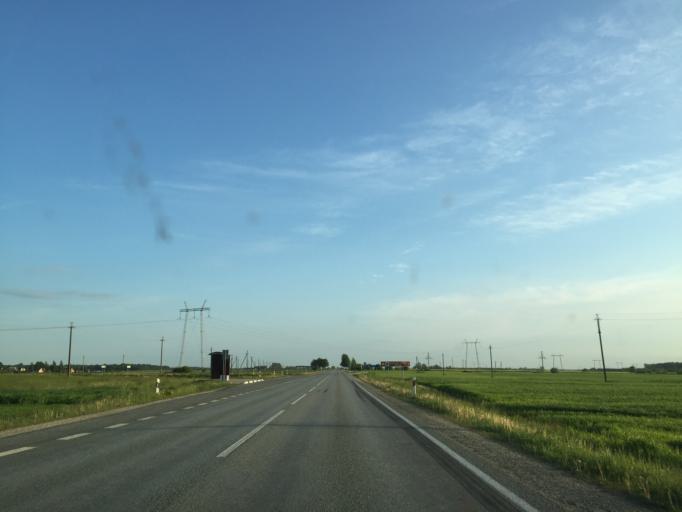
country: LT
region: Siauliu apskritis
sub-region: Joniskis
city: Joniskis
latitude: 56.1112
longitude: 23.4897
